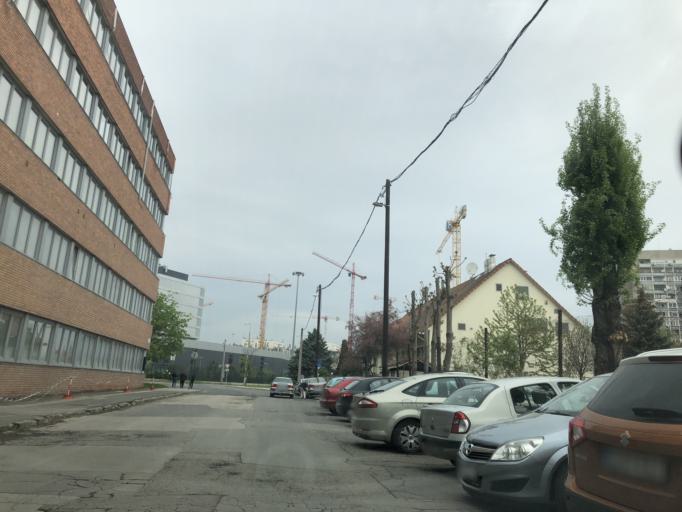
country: HU
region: Budapest
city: Budapest XI. keruelet
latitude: 47.4606
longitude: 19.0260
